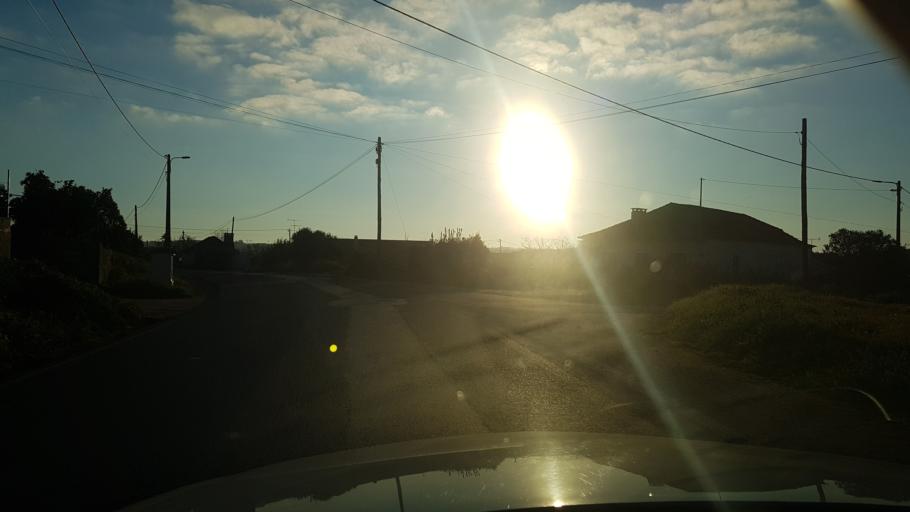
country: PT
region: Santarem
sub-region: Torres Novas
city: Torres Novas
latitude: 39.5544
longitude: -8.5673
